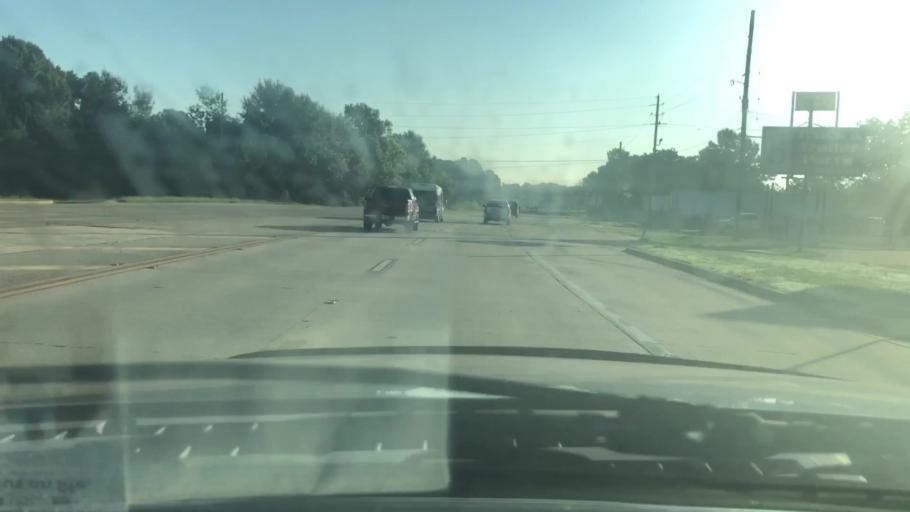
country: US
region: Texas
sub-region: Bowie County
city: Wake Village
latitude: 33.3954
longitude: -94.0967
